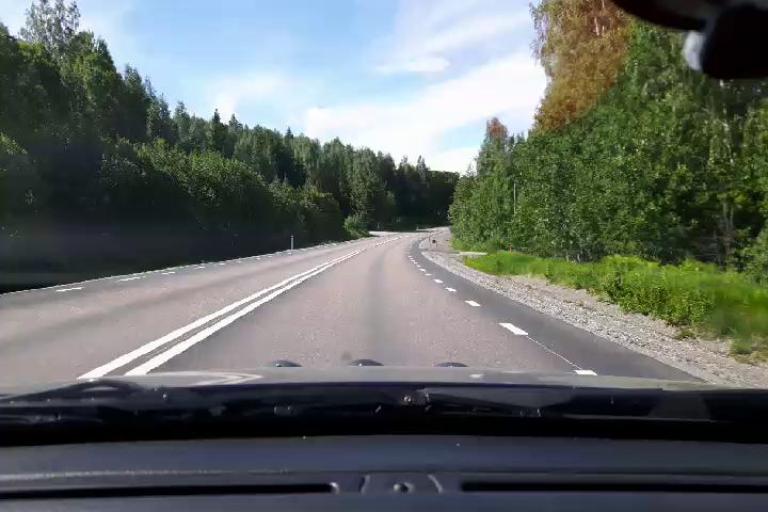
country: SE
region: Gaevleborg
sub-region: Bollnas Kommun
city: Kilafors
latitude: 61.1874
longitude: 16.7756
